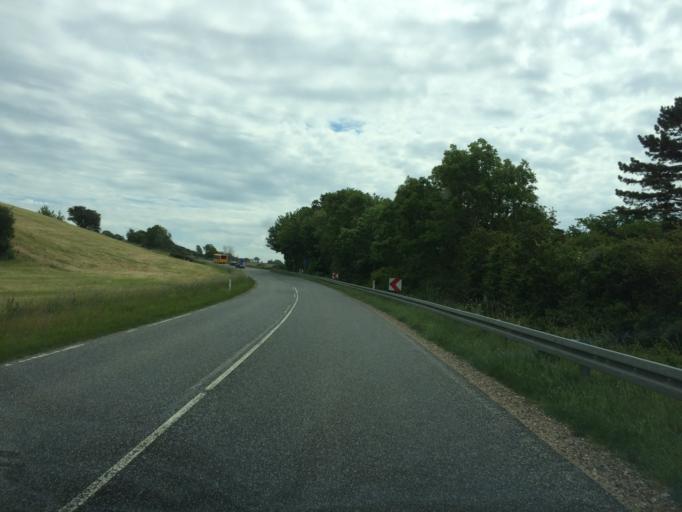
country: DK
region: Zealand
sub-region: Odsherred Kommune
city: Hojby
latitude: 55.9522
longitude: 11.4789
